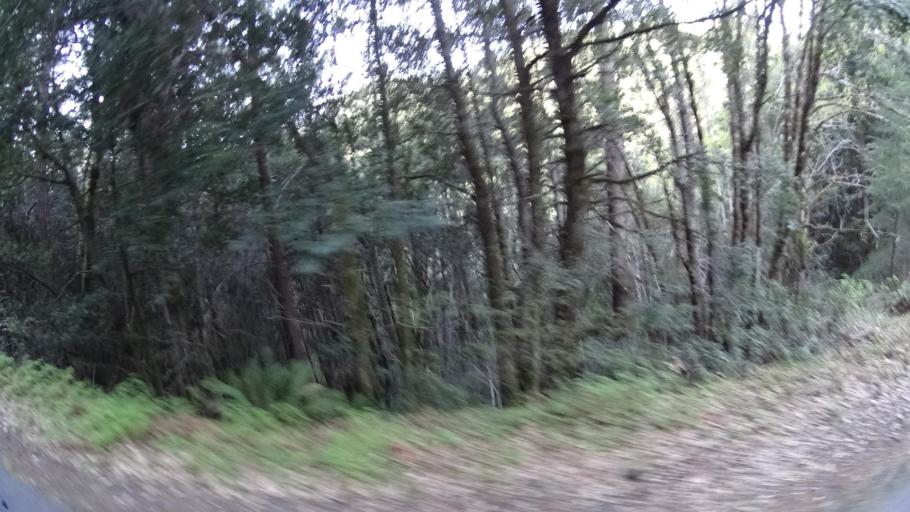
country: US
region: California
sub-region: Humboldt County
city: Bayside
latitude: 40.6951
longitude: -123.9423
